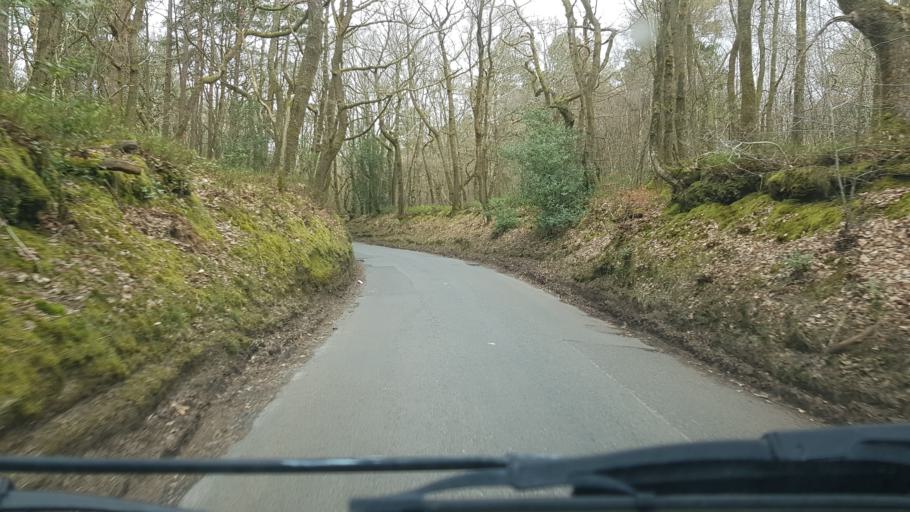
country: GB
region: England
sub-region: Surrey
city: Cranleigh
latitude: 51.1821
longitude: -0.4613
